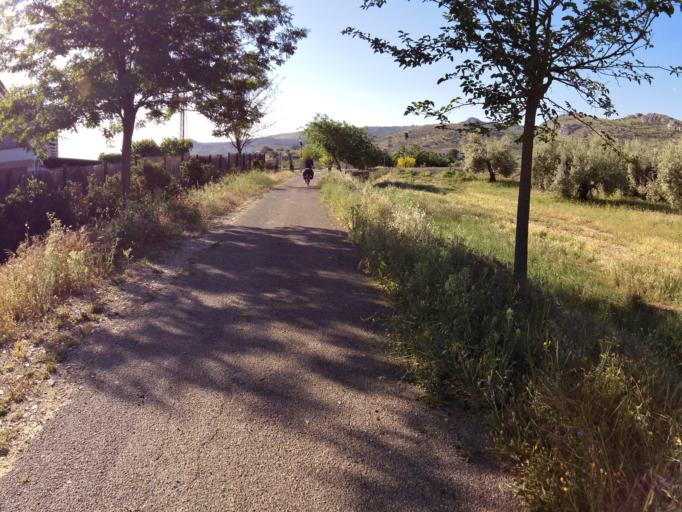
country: ES
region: Andalusia
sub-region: Province of Cordoba
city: Luque
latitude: 37.5712
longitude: -4.2559
